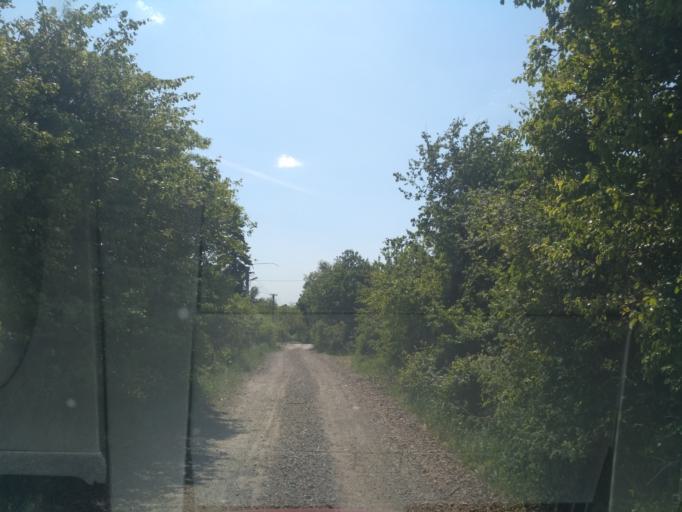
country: SK
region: Kosicky
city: Kosice
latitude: 48.8303
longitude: 21.4504
